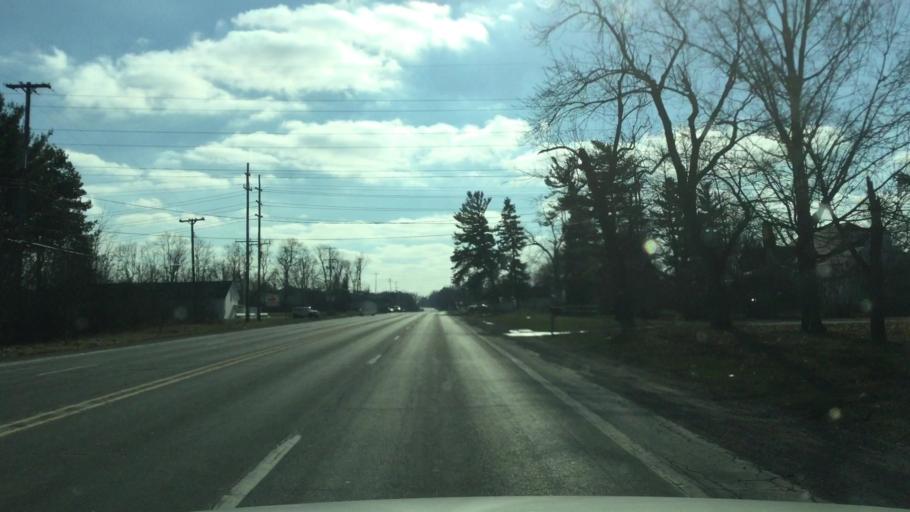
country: US
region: Michigan
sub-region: Genesee County
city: Beecher
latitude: 43.0929
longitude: -83.6748
